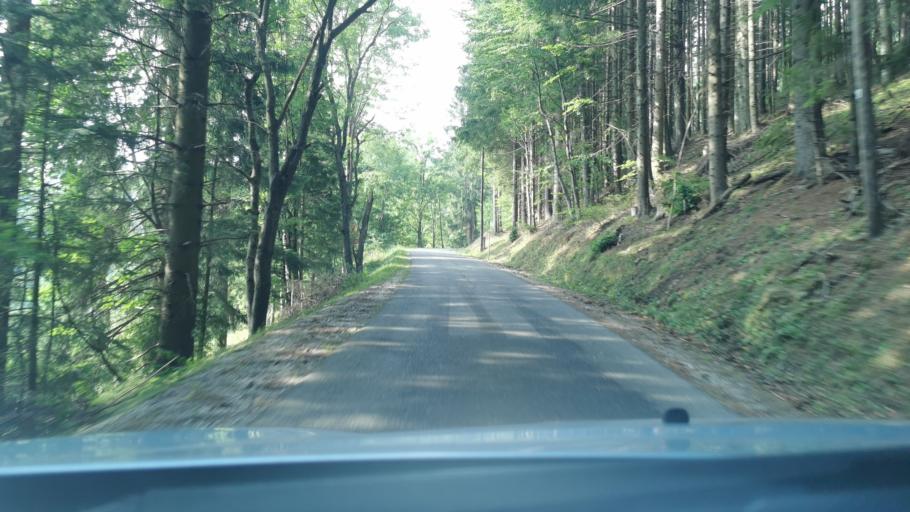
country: AT
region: Styria
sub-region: Politischer Bezirk Weiz
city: Fischbach
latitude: 47.3948
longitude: 15.6296
